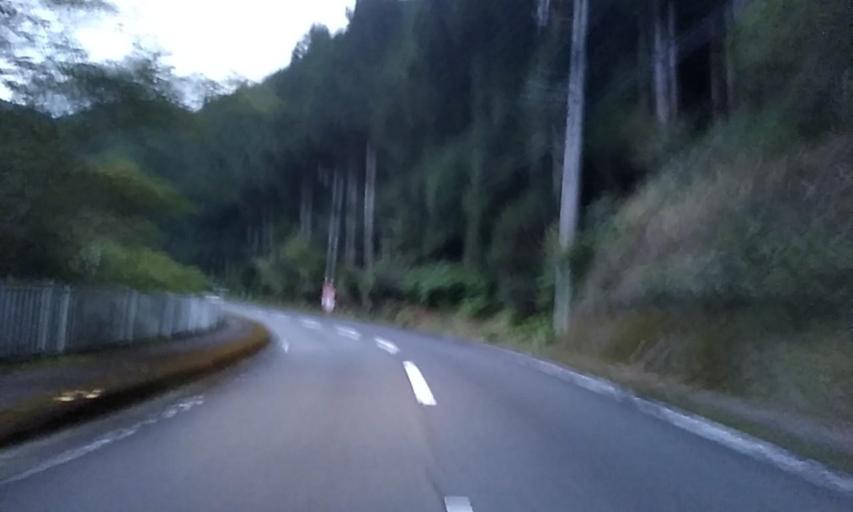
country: JP
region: Wakayama
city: Shingu
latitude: 33.7404
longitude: 135.9333
